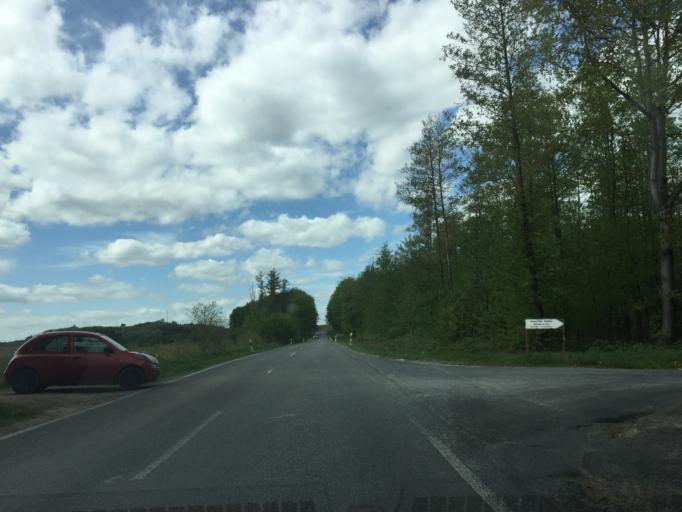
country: DE
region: Rheinland-Pfalz
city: Berod bei Wallmerod
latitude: 50.4837
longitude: 7.9220
